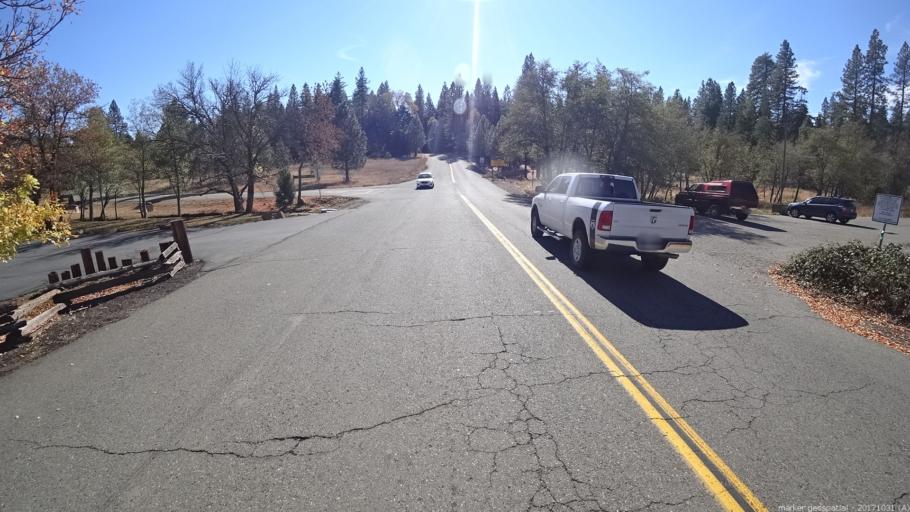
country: US
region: California
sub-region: Shasta County
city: Shingletown
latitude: 40.4922
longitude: -121.8872
